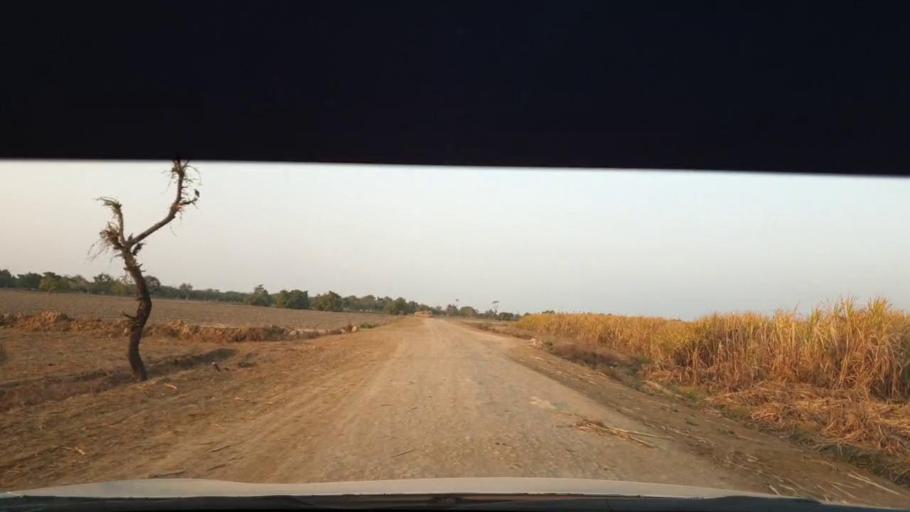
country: PK
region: Sindh
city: Berani
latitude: 25.7561
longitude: 69.0073
